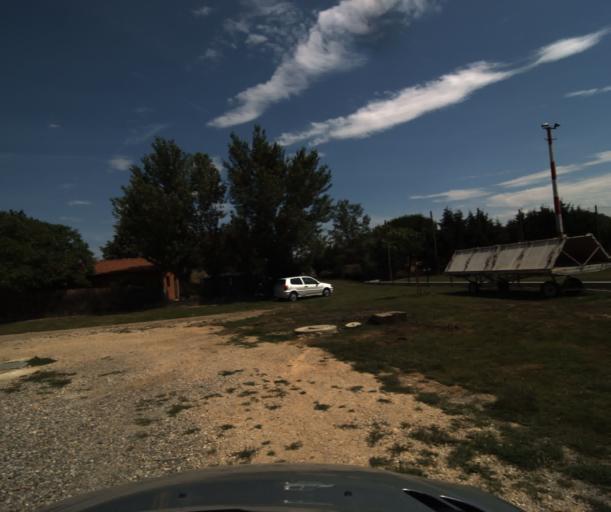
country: FR
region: Midi-Pyrenees
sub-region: Departement de la Haute-Garonne
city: Labastidette
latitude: 43.4570
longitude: 1.2445
